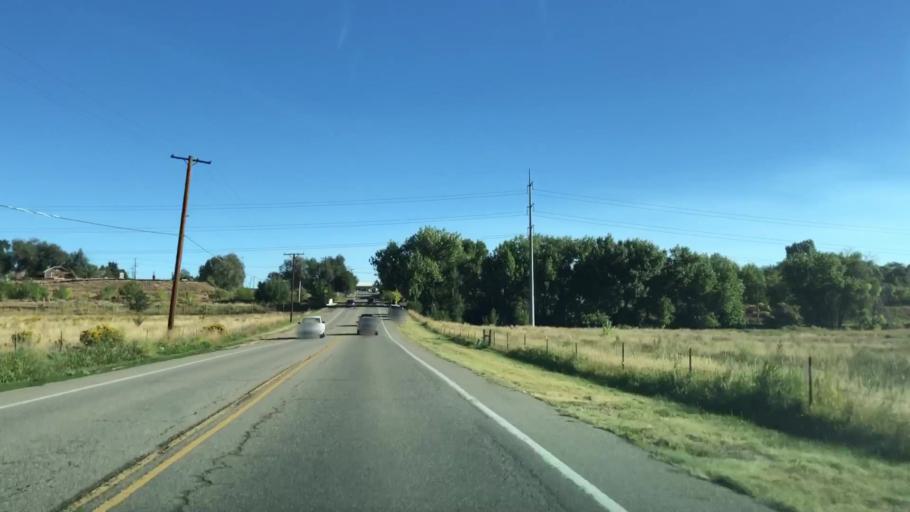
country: US
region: Colorado
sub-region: Larimer County
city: Loveland
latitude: 40.4038
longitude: -105.1220
